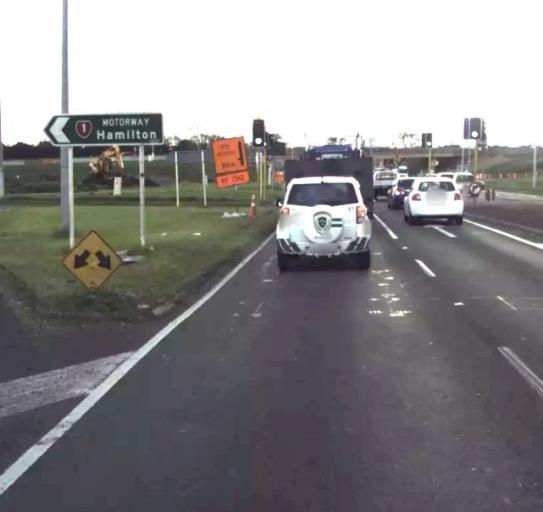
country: NZ
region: Auckland
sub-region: Auckland
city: Takanini
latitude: -37.0379
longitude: 174.9121
